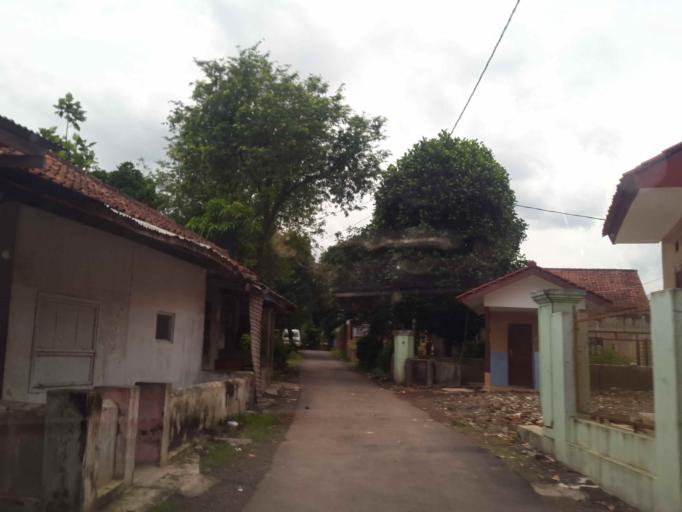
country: ID
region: West Java
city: Ciranjang-hilir
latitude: -6.8181
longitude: 107.2815
